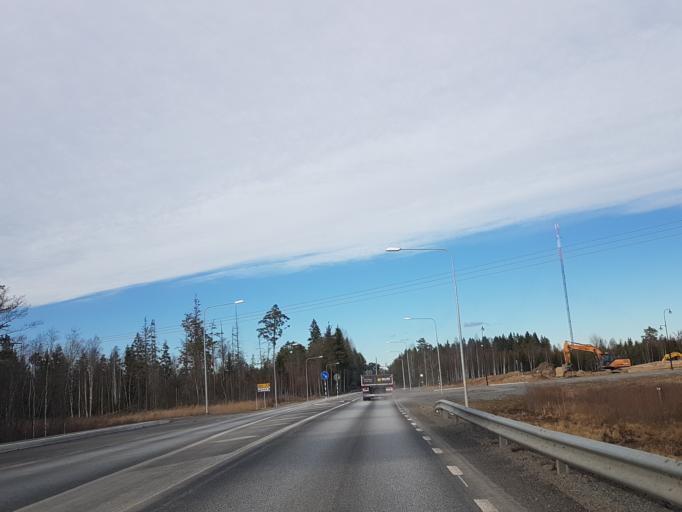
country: SE
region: Stockholm
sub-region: Norrtalje Kommun
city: Norrtalje
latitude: 59.7119
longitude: 18.6680
